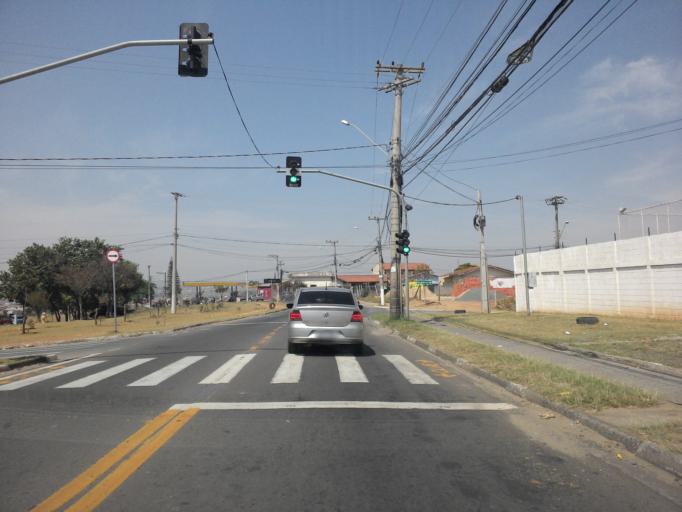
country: BR
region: Sao Paulo
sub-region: Hortolandia
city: Hortolandia
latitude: -22.9410
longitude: -47.1835
